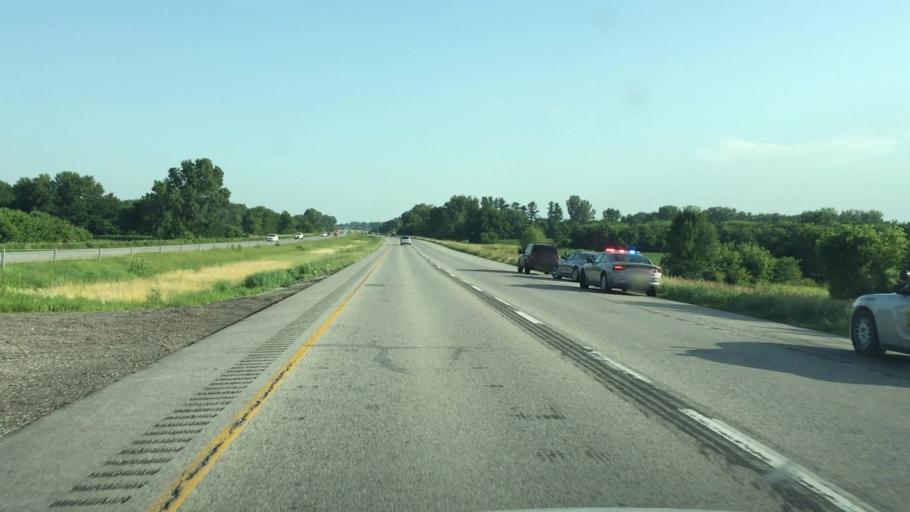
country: US
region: Iowa
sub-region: Johnson County
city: North Liberty
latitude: 41.7960
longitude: -91.6469
